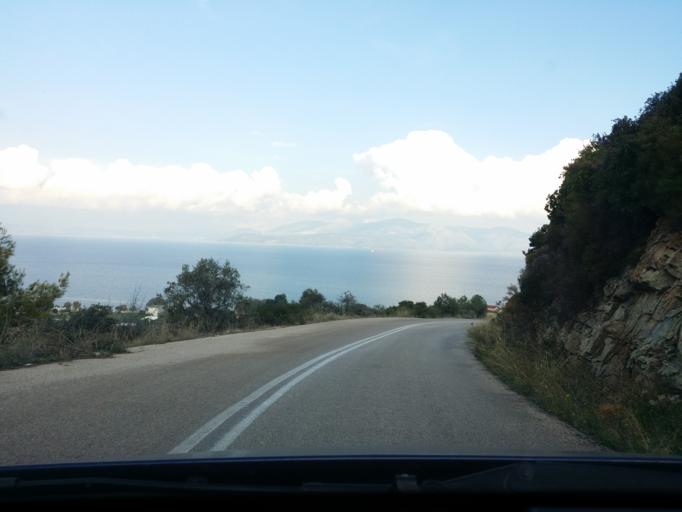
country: GR
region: Attica
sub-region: Nomarchia Anatolikis Attikis
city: Varnavas
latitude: 38.2661
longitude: 23.9672
